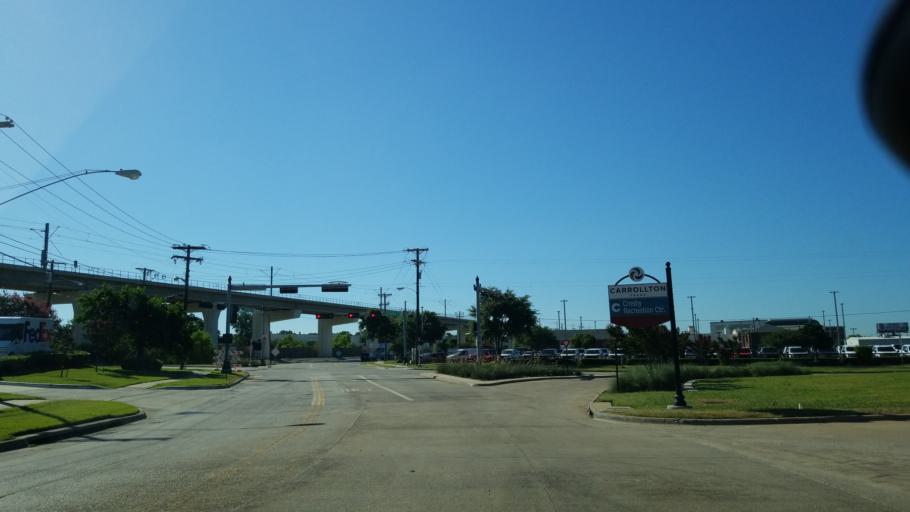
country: US
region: Texas
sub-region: Dallas County
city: Carrollton
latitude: 32.9482
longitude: -96.9051
